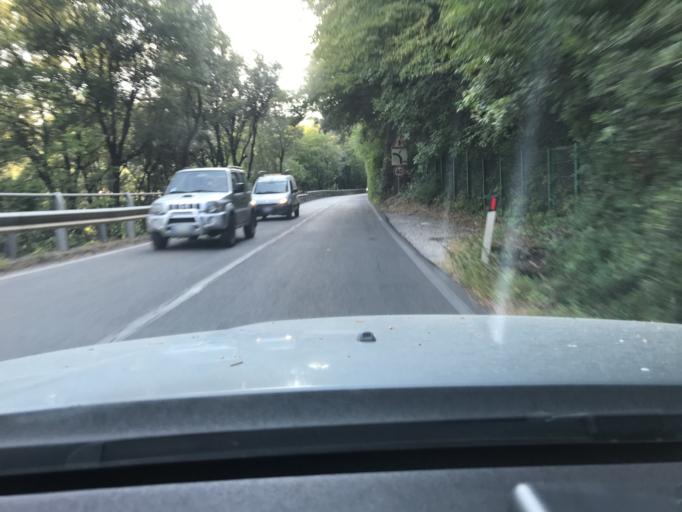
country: IT
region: Umbria
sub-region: Provincia di Terni
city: Amelia
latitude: 42.5594
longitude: 12.4100
